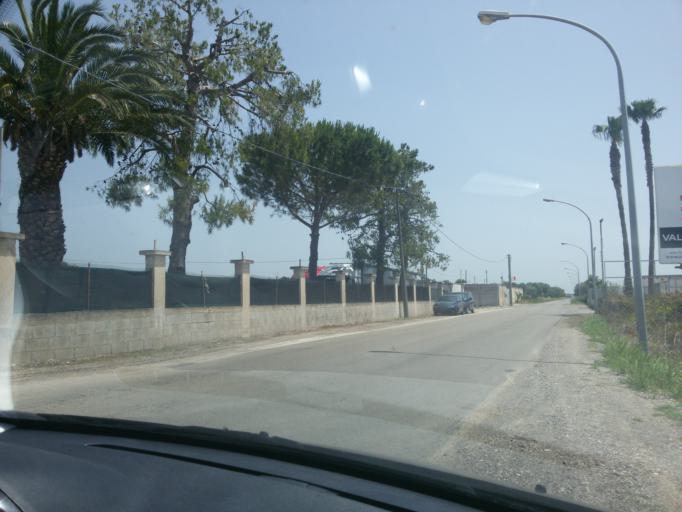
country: IT
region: Apulia
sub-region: Provincia di Brindisi
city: Mesagne
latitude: 40.5501
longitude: 17.8167
